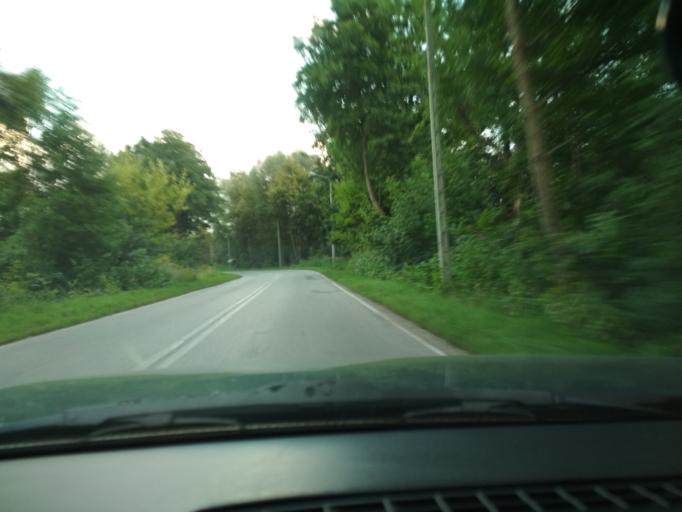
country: PL
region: Silesian Voivodeship
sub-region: Powiat cieszynski
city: Strumien
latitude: 49.9090
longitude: 18.7689
